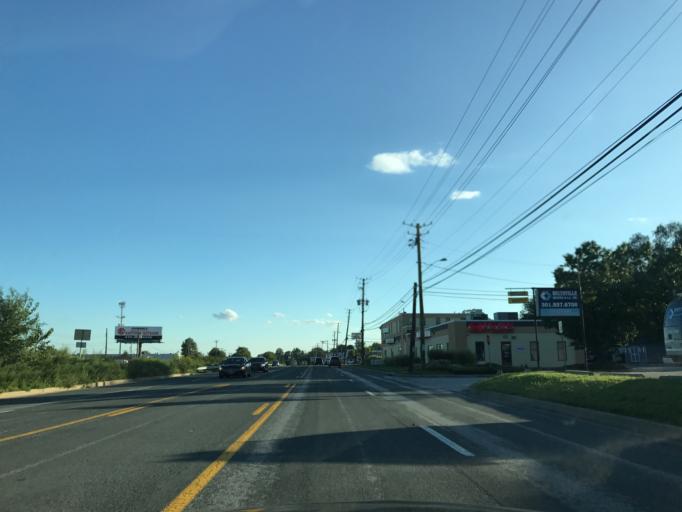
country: US
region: Maryland
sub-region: Prince George's County
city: Beltsville
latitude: 39.0448
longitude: -76.9023
